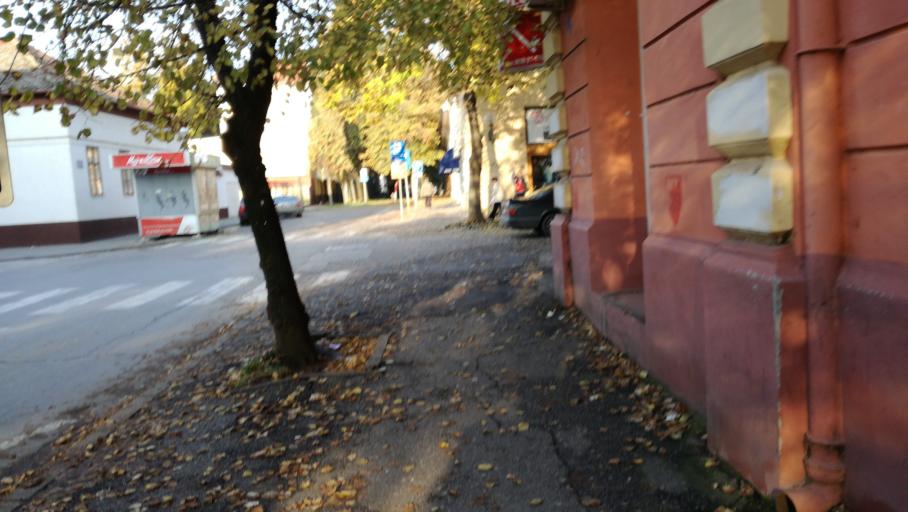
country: RS
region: Autonomna Pokrajina Vojvodina
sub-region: Severnobanatski Okrug
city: Kikinda
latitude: 45.8303
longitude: 20.4637
